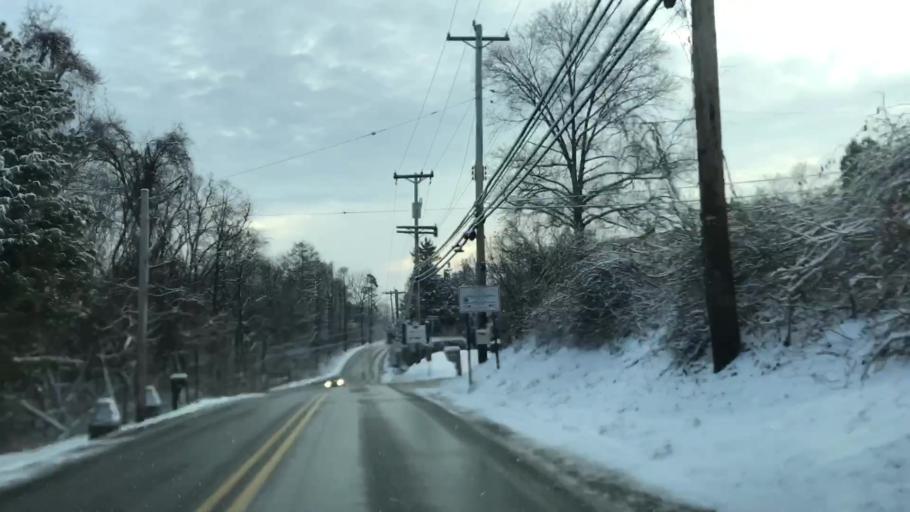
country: US
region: Pennsylvania
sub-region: Allegheny County
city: West View
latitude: 40.5455
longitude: -80.0645
